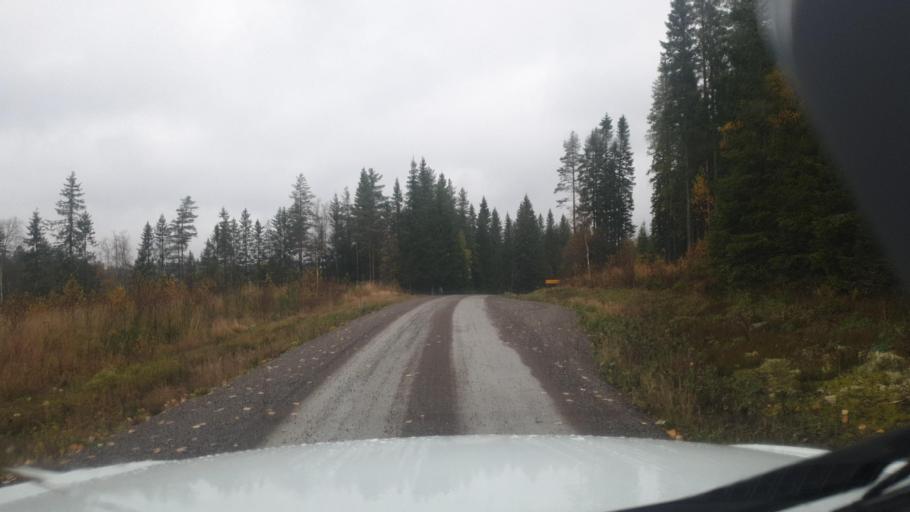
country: SE
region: Vaermland
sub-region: Eda Kommun
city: Charlottenberg
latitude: 60.0586
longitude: 12.6252
